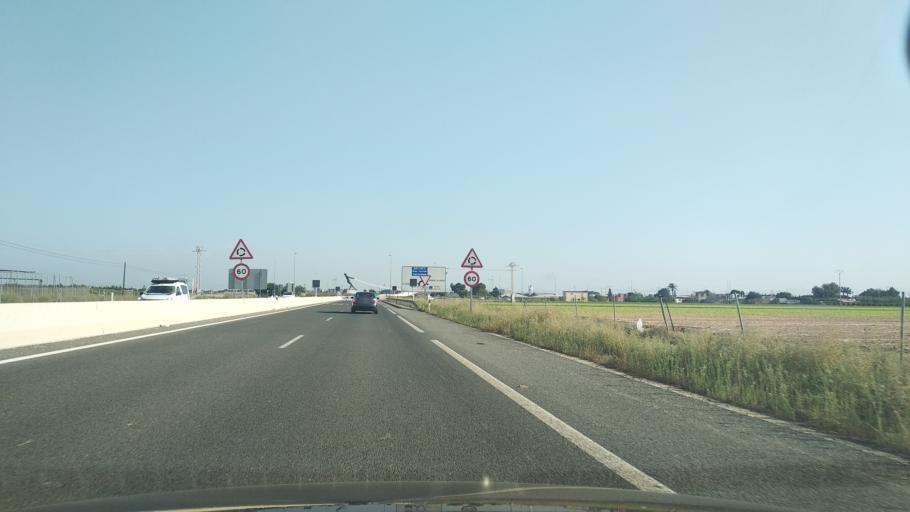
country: ES
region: Murcia
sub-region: Murcia
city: San Javier
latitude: 37.8233
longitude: -0.8514
